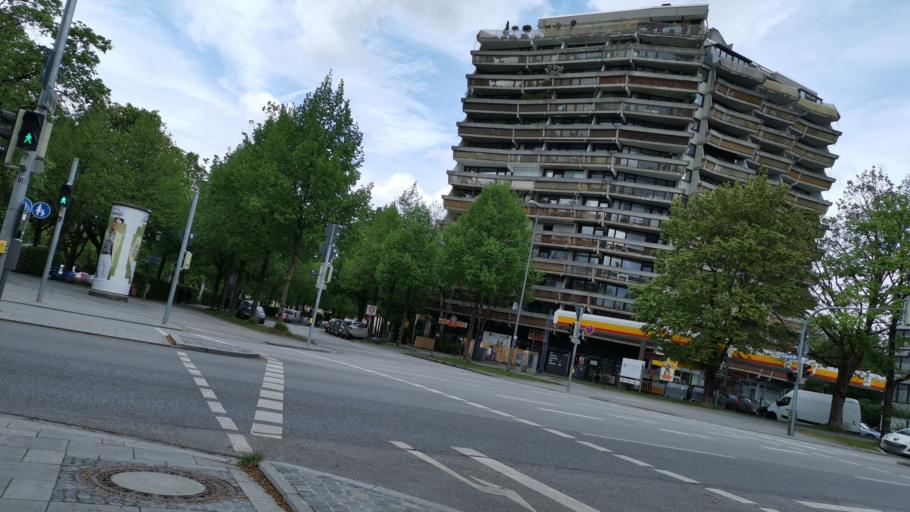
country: DE
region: Bavaria
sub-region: Upper Bavaria
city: Bogenhausen
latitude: 48.1707
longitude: 11.5948
